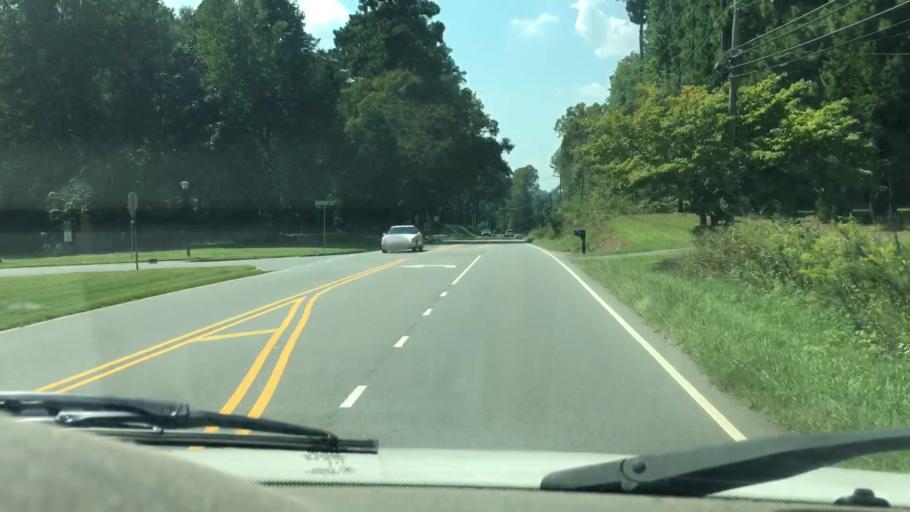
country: US
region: North Carolina
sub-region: Mecklenburg County
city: Huntersville
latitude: 35.3498
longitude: -80.8799
